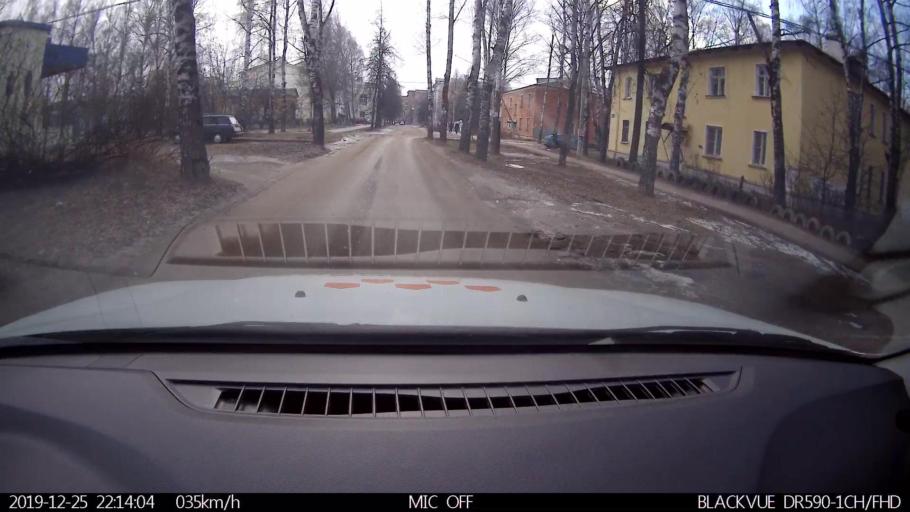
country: RU
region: Nizjnij Novgorod
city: Gorbatovka
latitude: 56.3326
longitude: 43.8465
